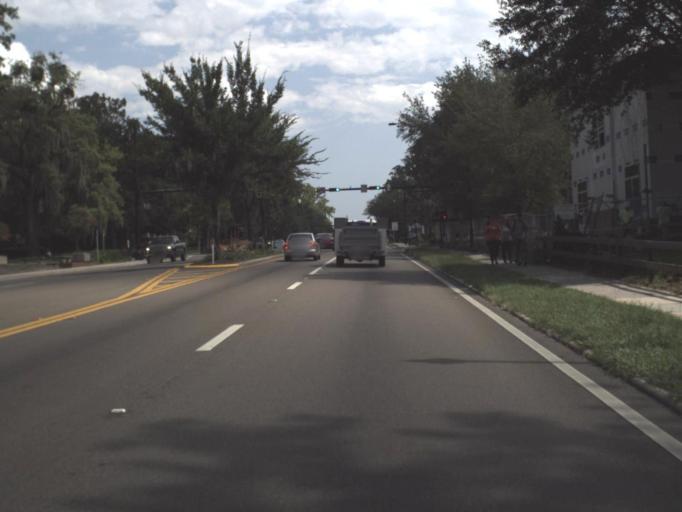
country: US
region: Florida
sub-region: Alachua County
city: Gainesville
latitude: 29.6477
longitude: -82.3393
